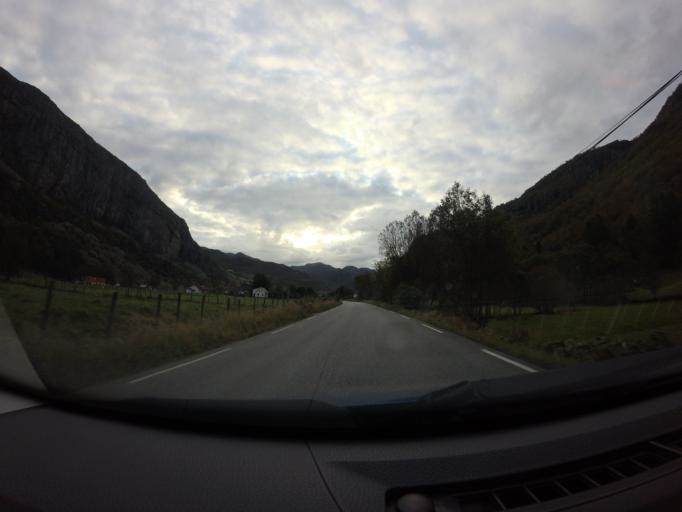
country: NO
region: Rogaland
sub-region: Forsand
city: Forsand
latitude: 58.8082
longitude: 6.2395
